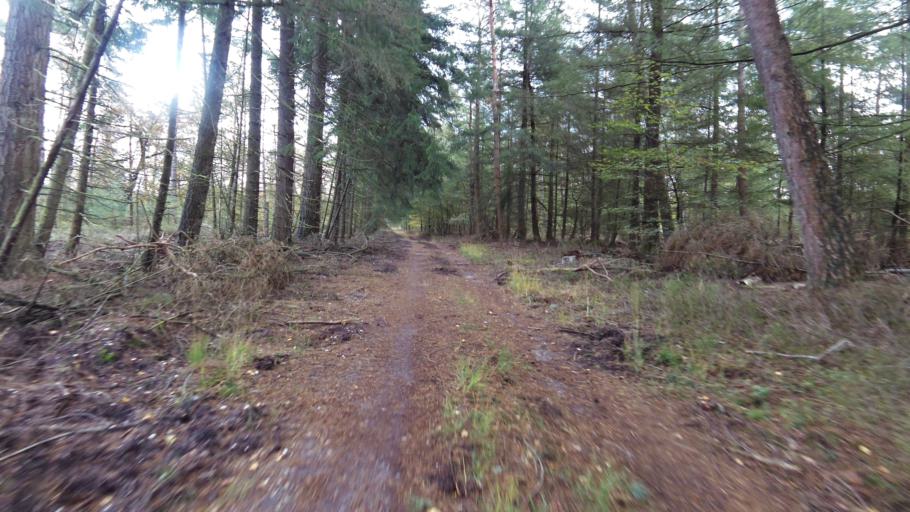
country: NL
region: Gelderland
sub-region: Gemeente Apeldoorn
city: Uddel
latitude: 52.3008
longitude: 5.8208
